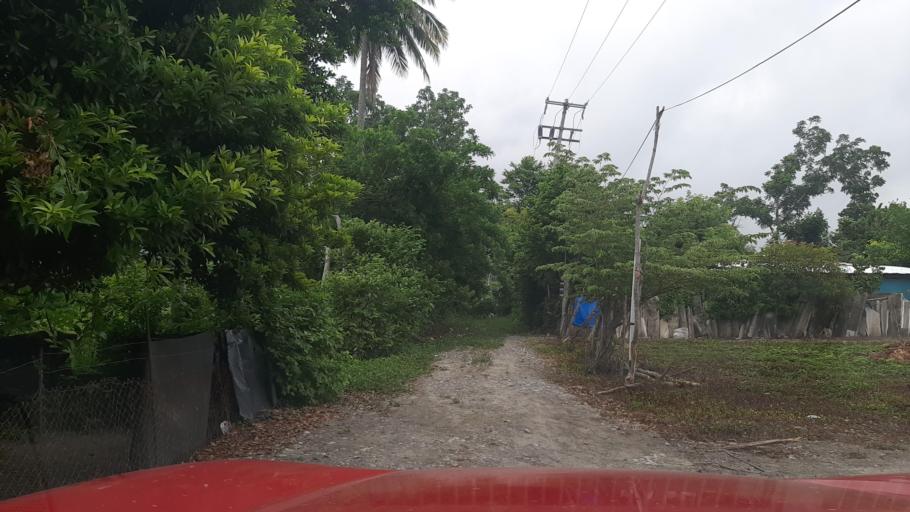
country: MX
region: Veracruz
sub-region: Papantla
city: Residencial Tajin
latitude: 20.6045
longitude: -97.4317
